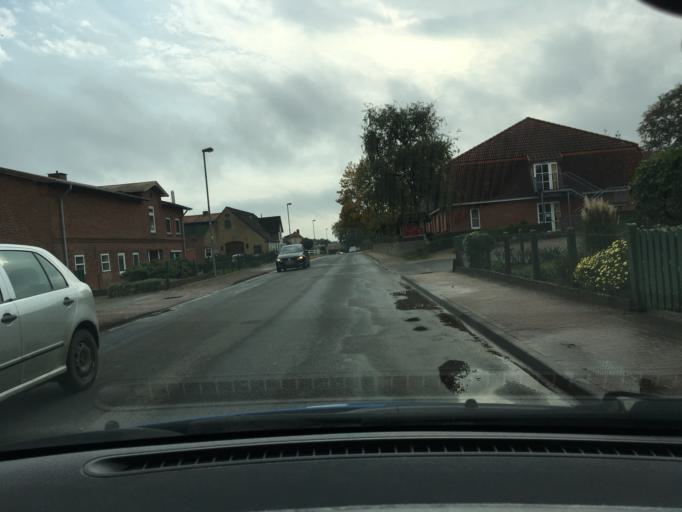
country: DE
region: Schleswig-Holstein
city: Tensfeld
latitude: 54.0447
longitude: 10.3178
